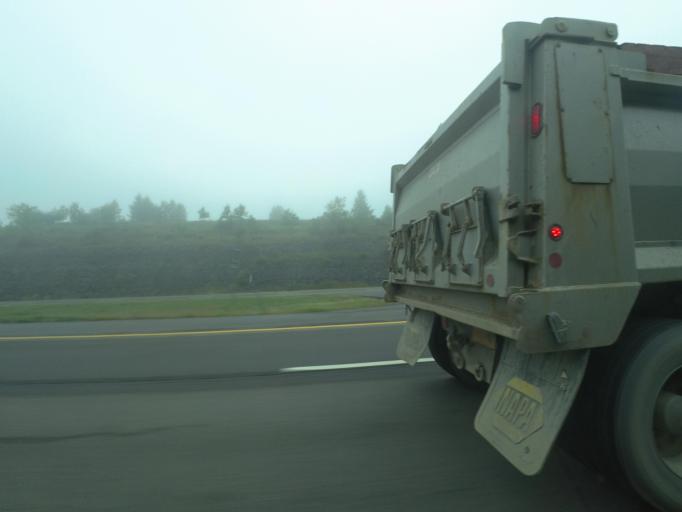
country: US
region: New York
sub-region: Broome County
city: Chenango Bridge
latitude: 42.1863
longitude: -75.7122
